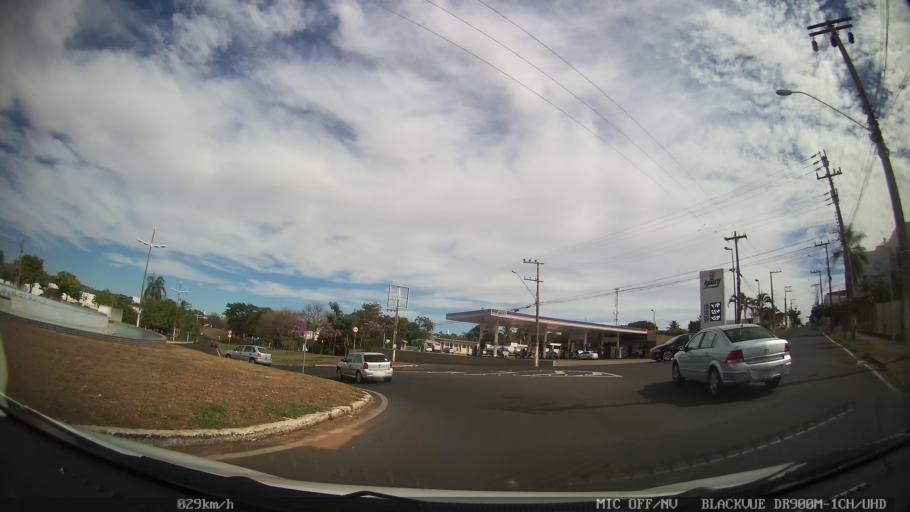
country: BR
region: Sao Paulo
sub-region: Catanduva
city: Catanduva
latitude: -21.1515
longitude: -48.9802
